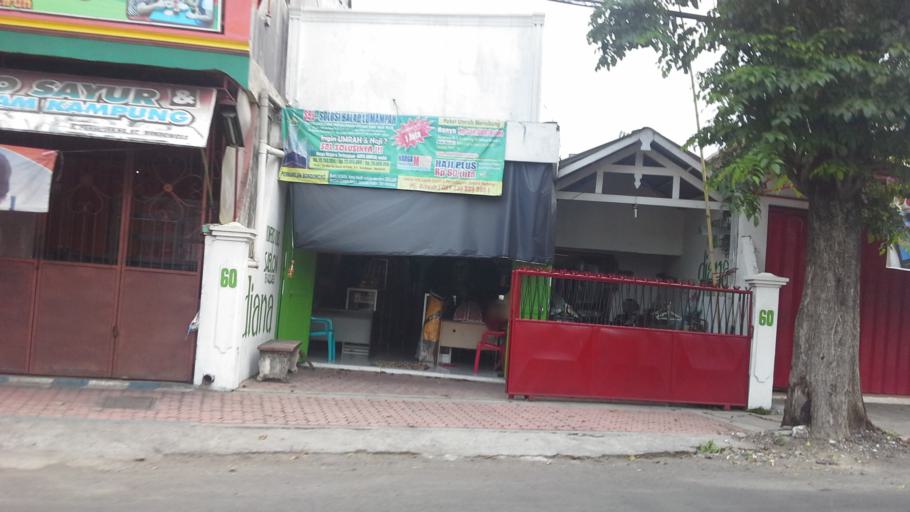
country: ID
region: East Java
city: Bondowoso
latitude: -7.9228
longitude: 113.8206
